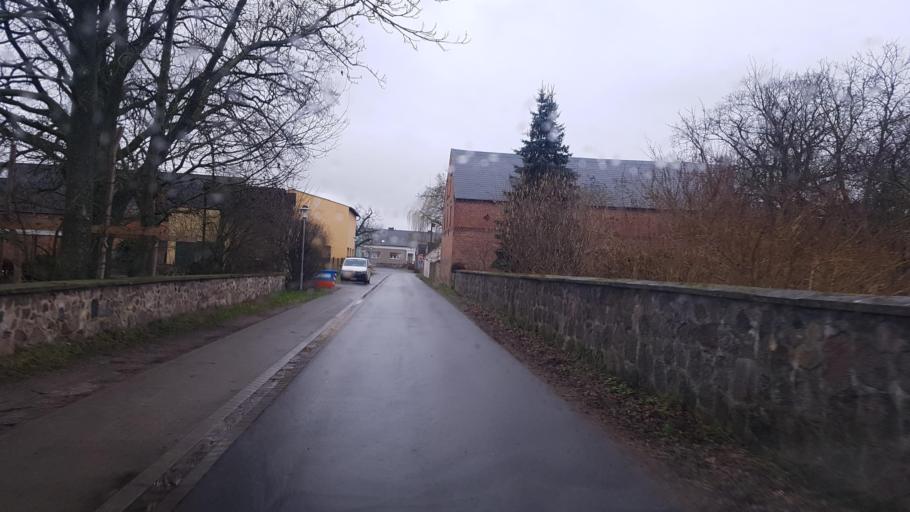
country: DE
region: Brandenburg
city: Oranienburg
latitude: 52.8747
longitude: 13.2222
